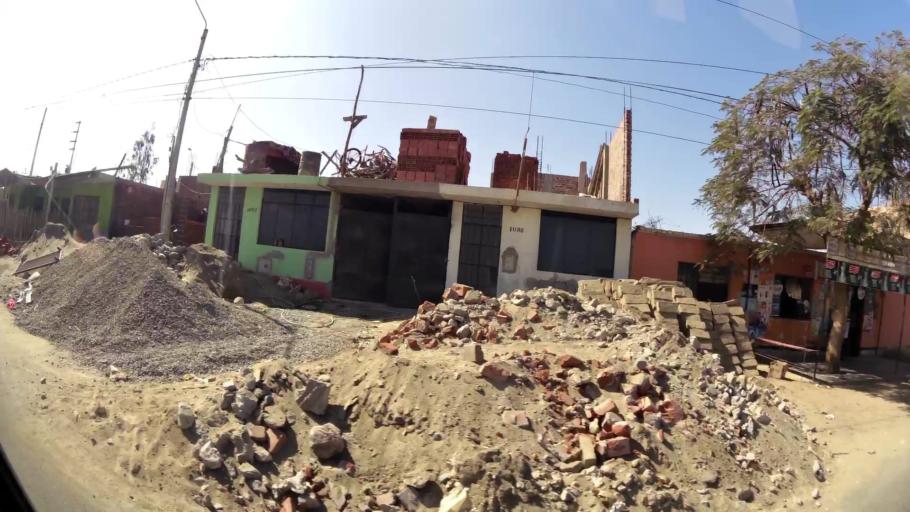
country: PE
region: Ica
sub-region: Provincia de Ica
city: La Tinguina
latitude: -14.0293
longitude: -75.7088
